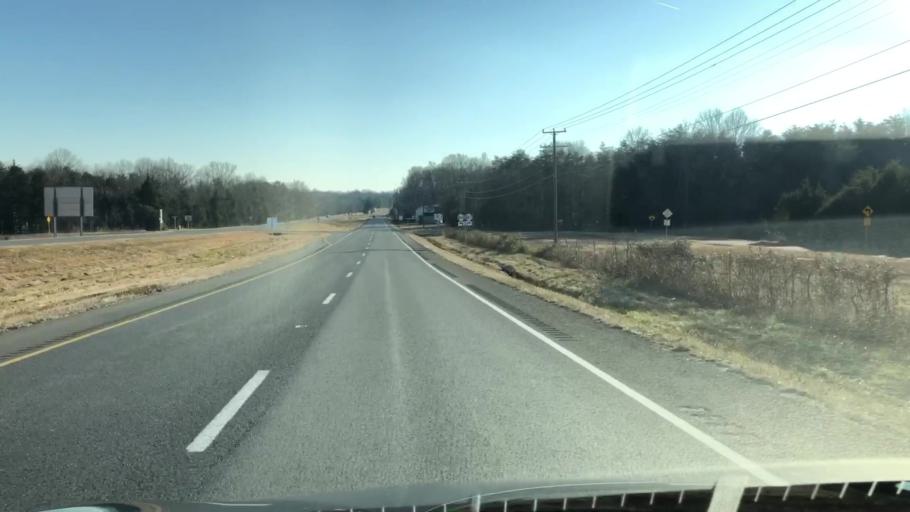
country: US
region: Virginia
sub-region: Fauquier County
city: Bealeton
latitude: 38.6089
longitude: -77.8005
